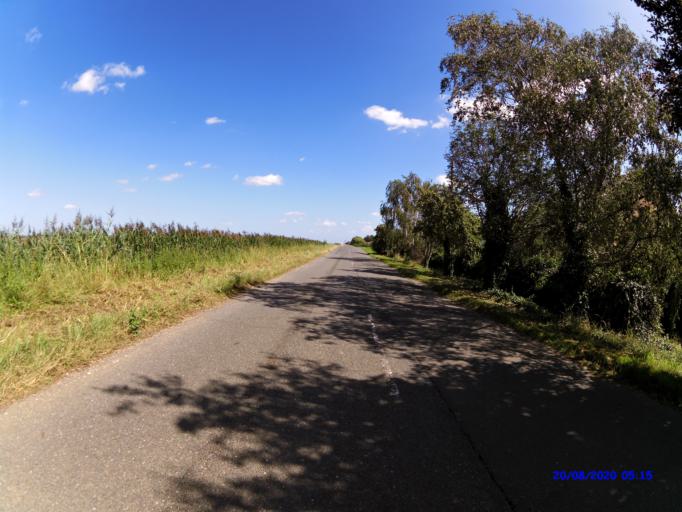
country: GB
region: England
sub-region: Cambridgeshire
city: Whittlesey
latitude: 52.5227
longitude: -0.1161
